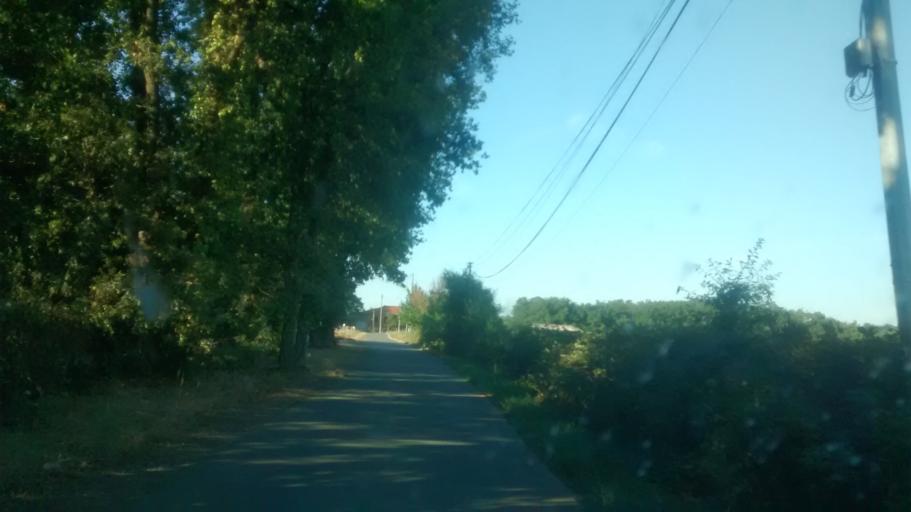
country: FR
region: Midi-Pyrenees
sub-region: Departement de la Haute-Garonne
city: Lherm
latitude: 43.4183
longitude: 1.2172
